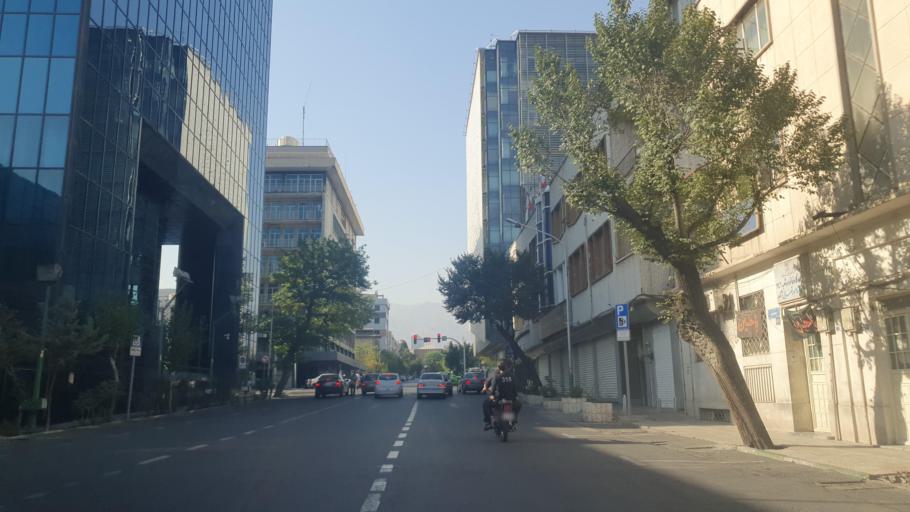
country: IR
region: Tehran
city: Tehran
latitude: 35.7061
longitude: 51.4211
